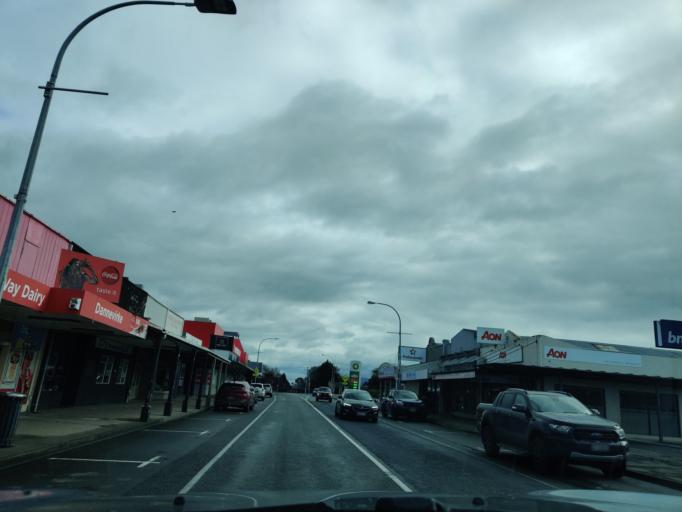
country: NZ
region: Manawatu-Wanganui
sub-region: Palmerston North City
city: Palmerston North
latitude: -40.2099
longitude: 176.0959
